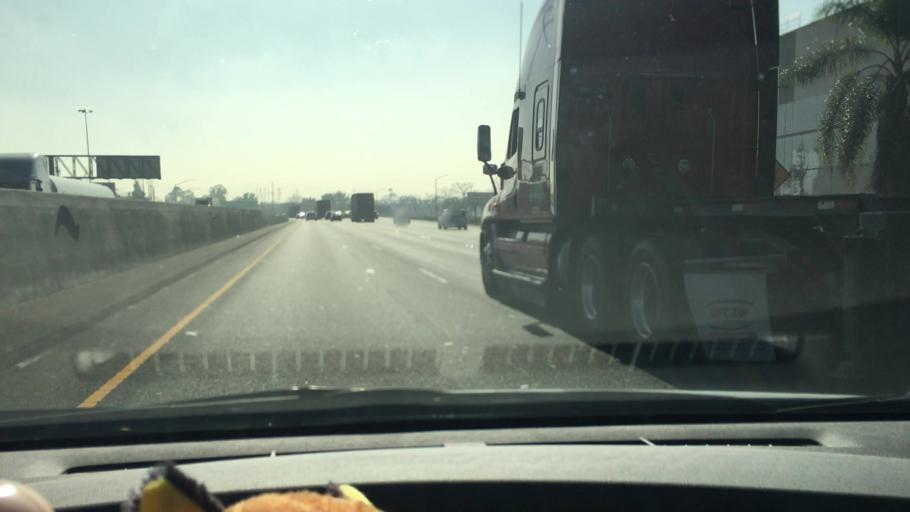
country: US
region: California
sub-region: Los Angeles County
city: Signal Hill
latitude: 33.8364
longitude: -118.2082
